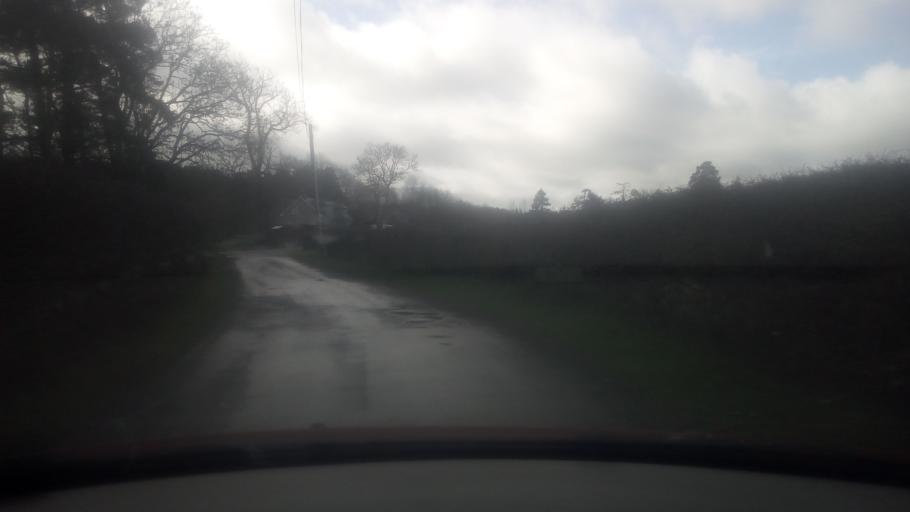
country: GB
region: Scotland
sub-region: The Scottish Borders
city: Saint Boswells
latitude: 55.5202
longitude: -2.6533
